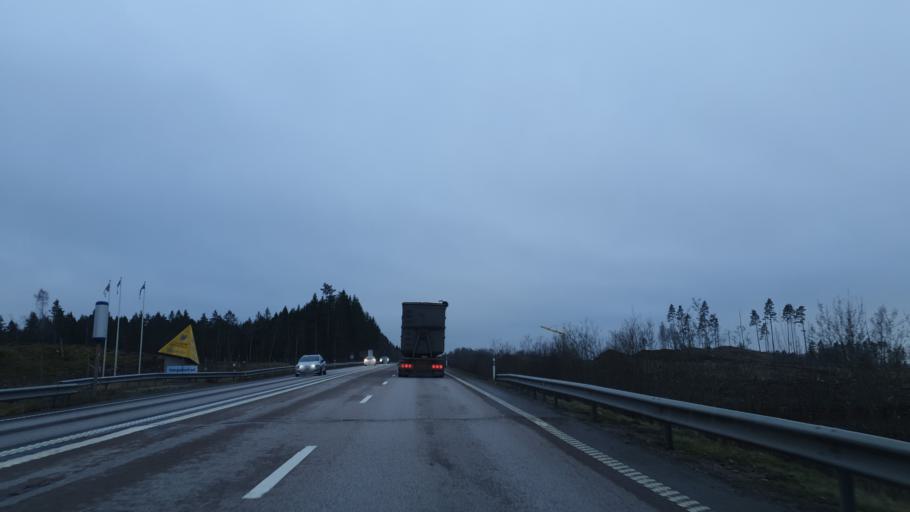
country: SE
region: Vaestra Goetaland
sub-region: Vargarda Kommun
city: Vargarda
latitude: 58.0194
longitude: 12.7795
